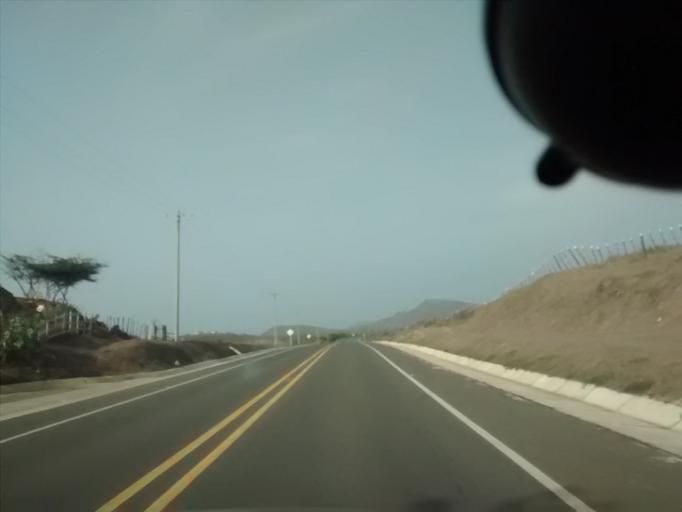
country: CO
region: Atlantico
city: Juan de Acosta
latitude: 10.8608
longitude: -75.1078
